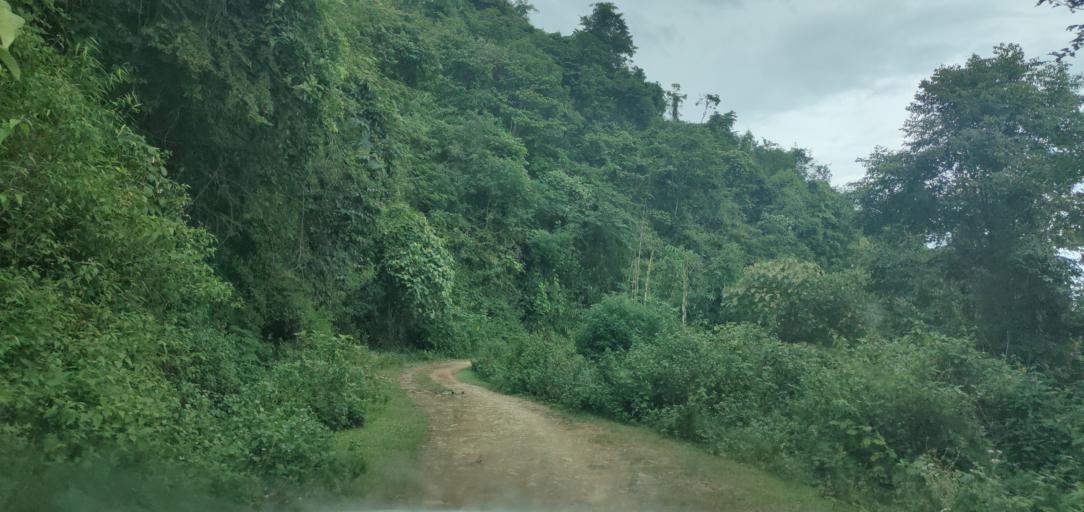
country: LA
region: Phongsali
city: Phongsali
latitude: 21.4464
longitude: 102.3150
